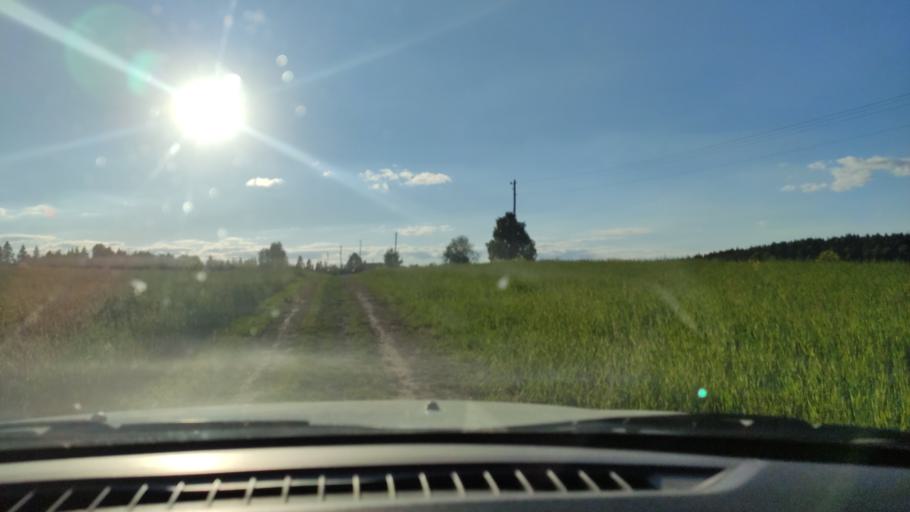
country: RU
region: Perm
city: Orda
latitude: 57.2925
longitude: 56.5820
